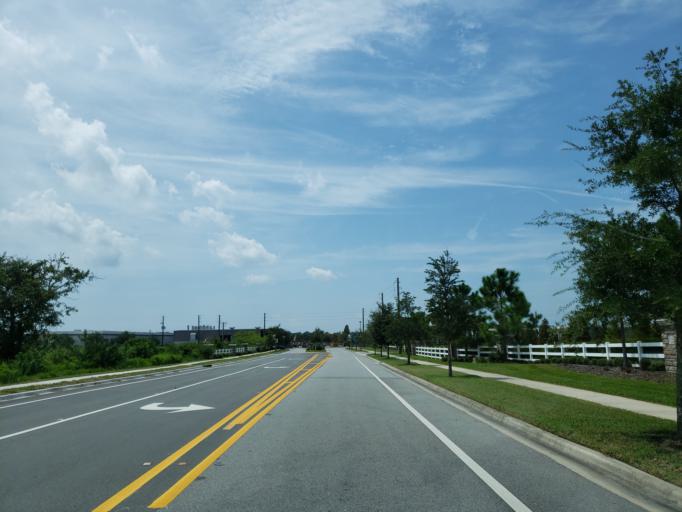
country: US
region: Florida
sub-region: Hillsborough County
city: Riverview
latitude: 27.8463
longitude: -82.3414
